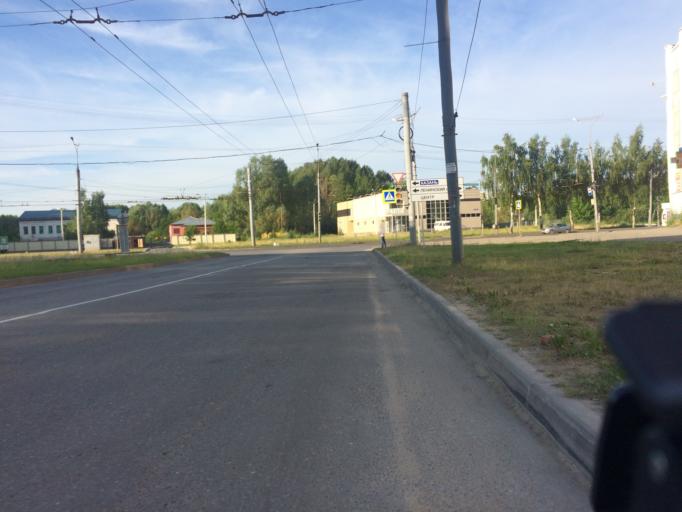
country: RU
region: Mariy-El
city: Yoshkar-Ola
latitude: 56.6272
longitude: 47.9152
